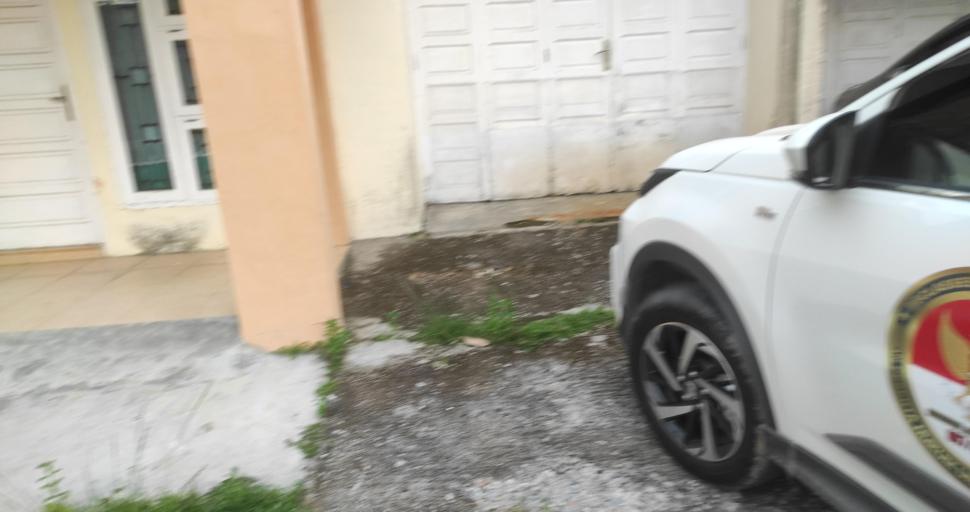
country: ID
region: West Sumatra
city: Sawahlunto
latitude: -0.6590
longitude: 100.7563
